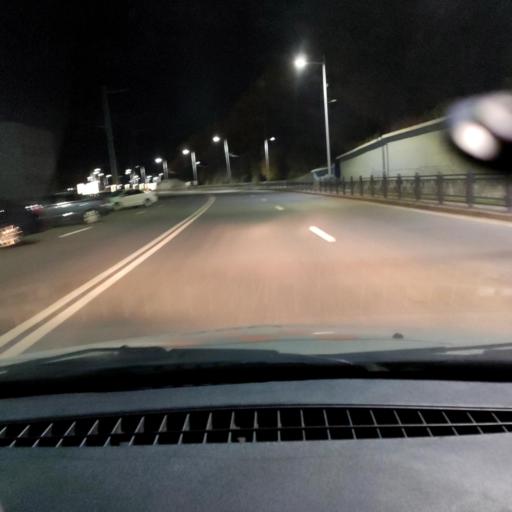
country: RU
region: Bashkortostan
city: Ufa
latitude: 54.7144
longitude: 55.9369
